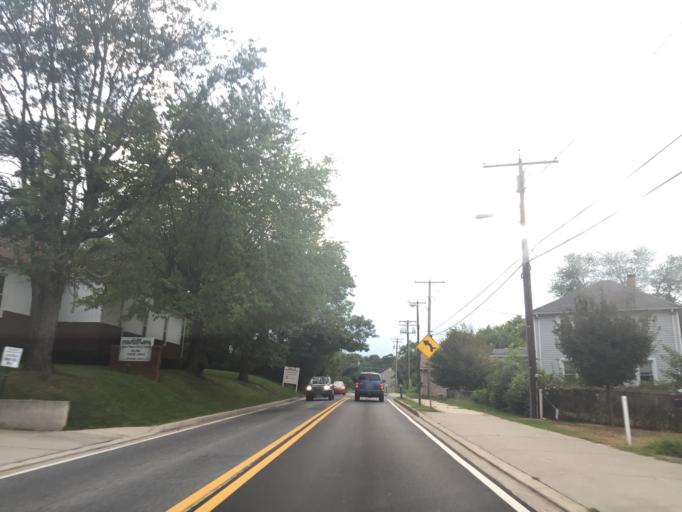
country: US
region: Maryland
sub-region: Anne Arundel County
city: Pumphrey
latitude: 39.2181
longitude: -76.6410
